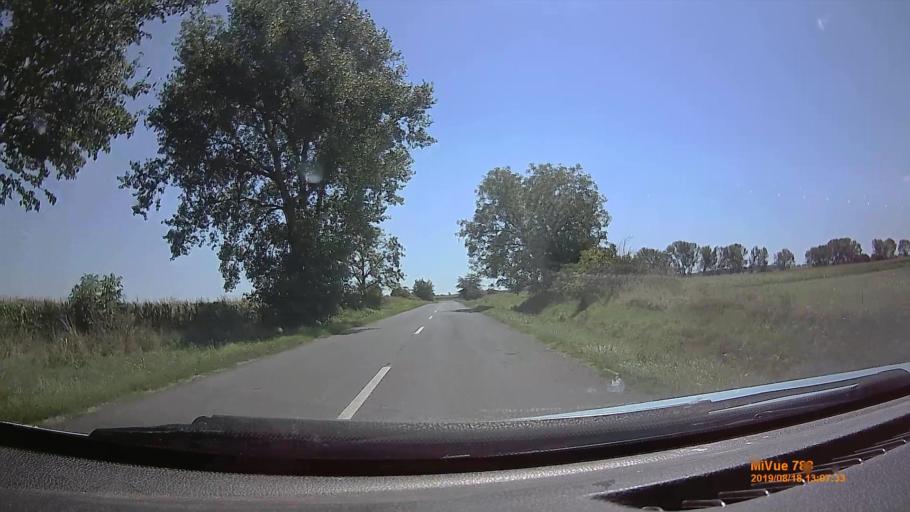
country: HU
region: Fejer
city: Kaloz
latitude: 46.9488
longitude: 18.4955
